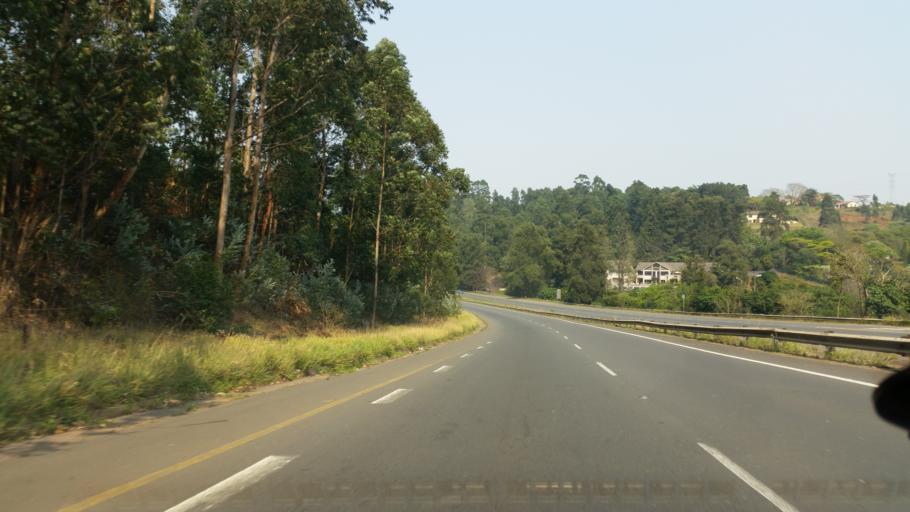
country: ZA
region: KwaZulu-Natal
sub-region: eThekwini Metropolitan Municipality
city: Mpumalanga
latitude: -29.7954
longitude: 30.7784
